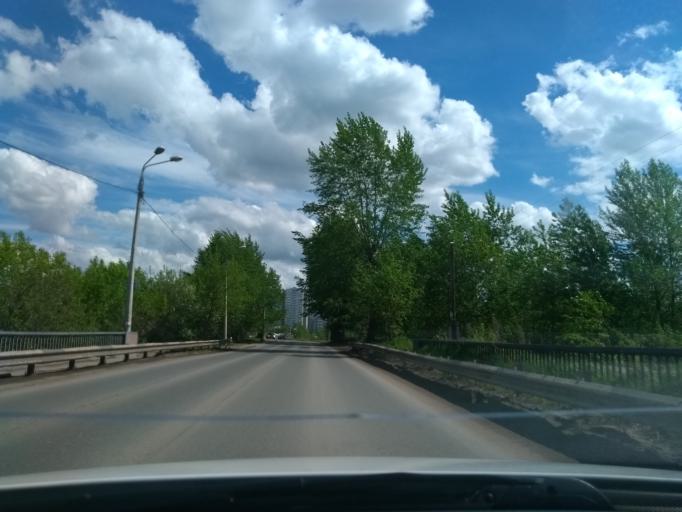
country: RU
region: Perm
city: Kondratovo
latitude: 58.0023
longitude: 56.1297
